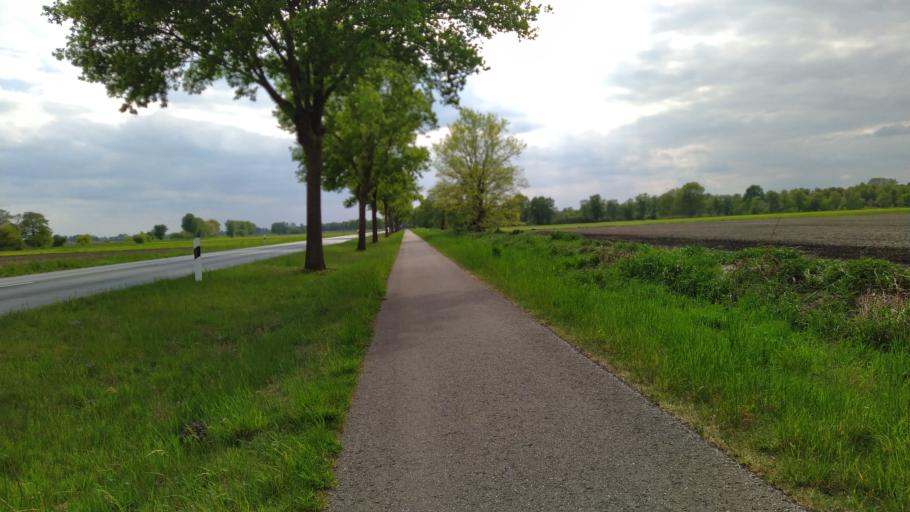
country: DE
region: Lower Saxony
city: Tarmstedt
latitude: 53.2128
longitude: 9.0486
